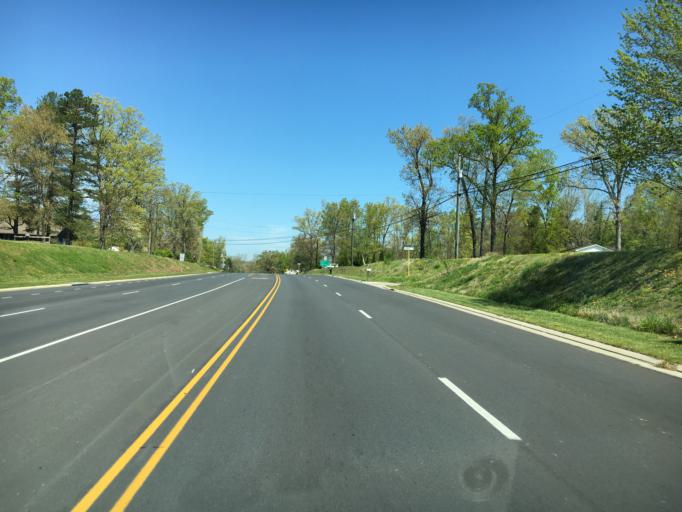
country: US
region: Virginia
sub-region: Augusta County
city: Crimora
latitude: 38.1545
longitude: -78.8429
